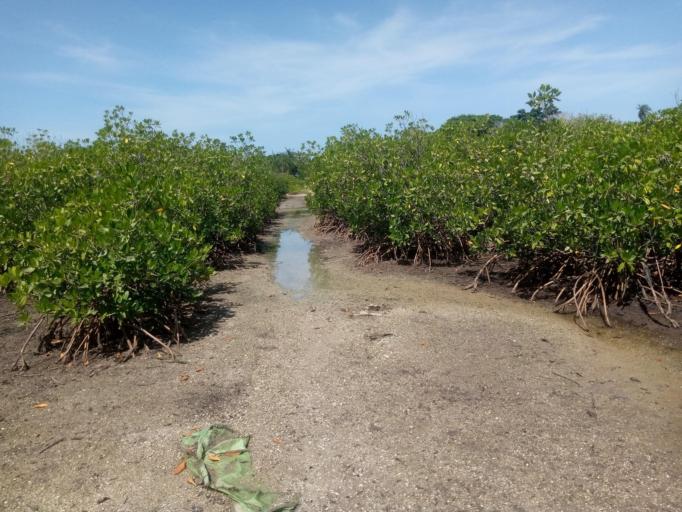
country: GM
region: Western
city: Gunjur
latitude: 13.0388
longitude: -16.7356
